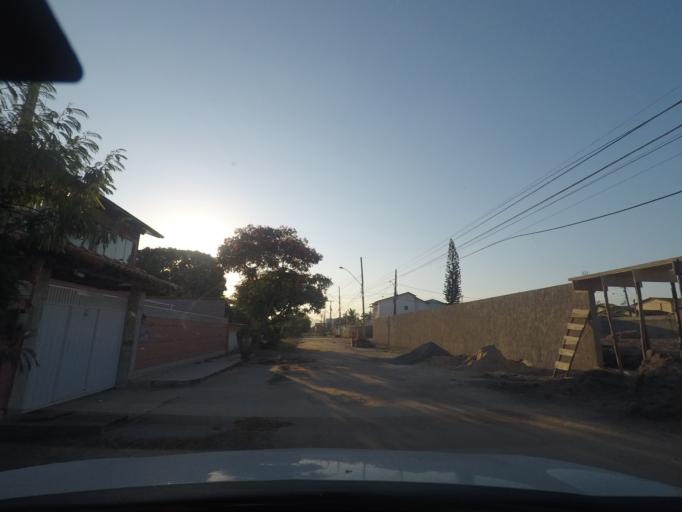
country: BR
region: Rio de Janeiro
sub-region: Marica
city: Marica
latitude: -22.9695
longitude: -42.9302
